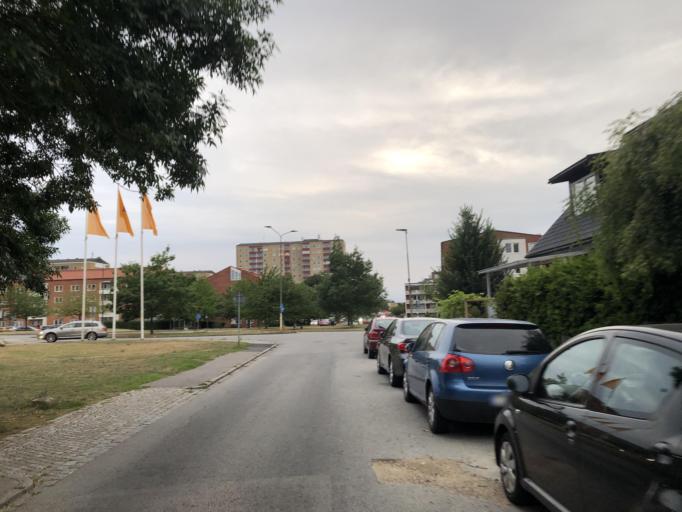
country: SE
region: Skane
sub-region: Malmo
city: Malmoe
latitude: 55.5734
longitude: 13.0253
